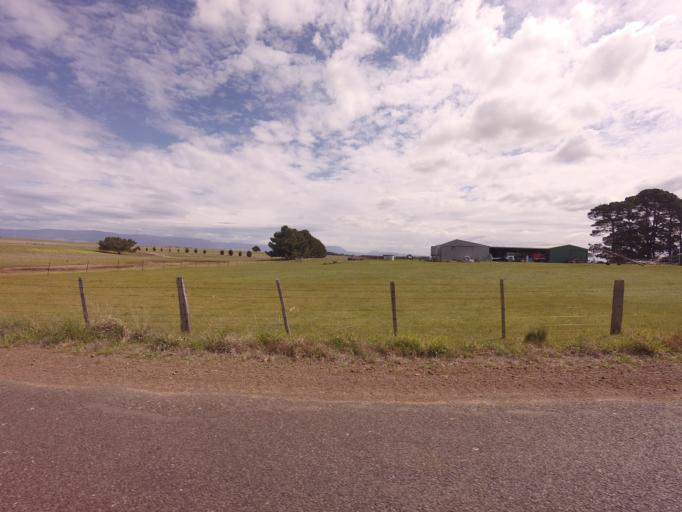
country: AU
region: Tasmania
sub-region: Northern Midlands
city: Longford
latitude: -41.6973
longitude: 147.1965
